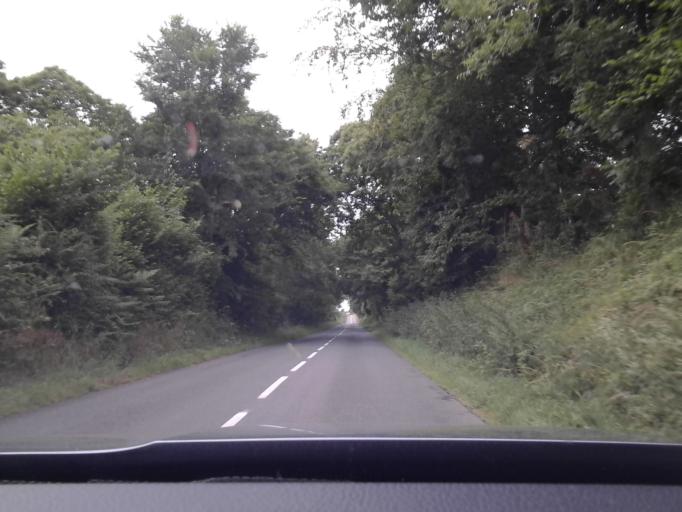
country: FR
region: Lower Normandy
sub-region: Departement de la Manche
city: Beaumont-Hague
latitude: 49.6725
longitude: -1.8282
